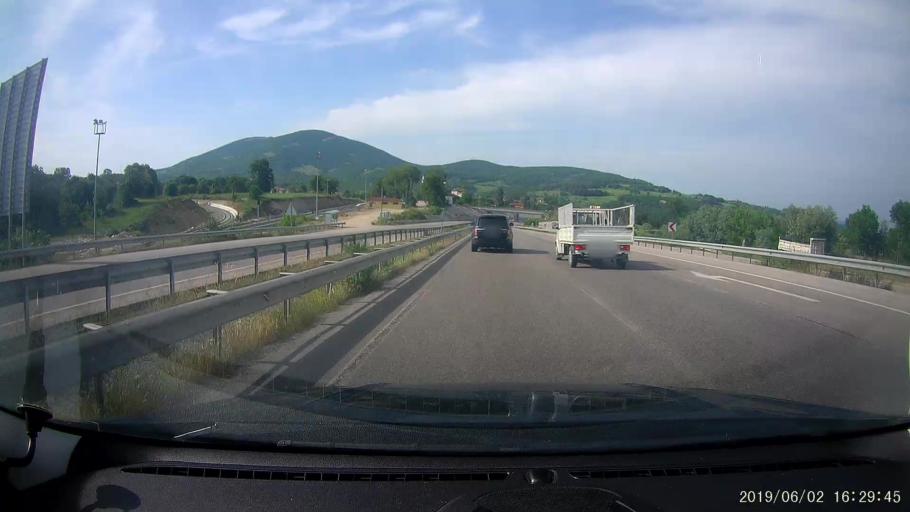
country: TR
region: Samsun
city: Ladik
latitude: 41.0167
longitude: 35.8723
